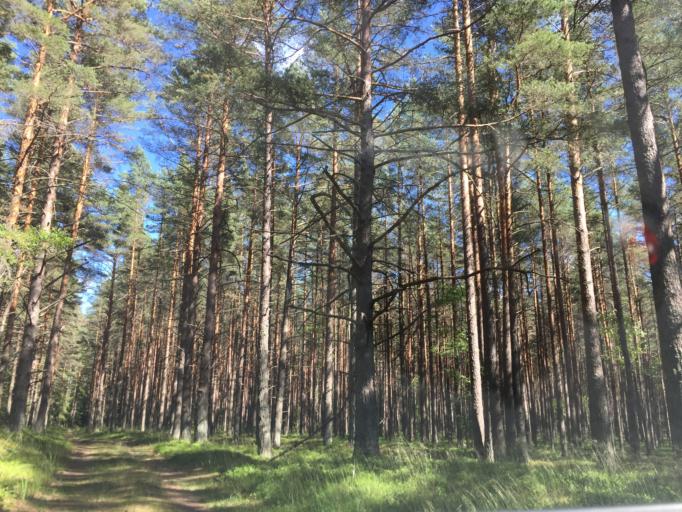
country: LV
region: Ventspils
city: Ventspils
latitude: 57.4716
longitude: 21.6484
